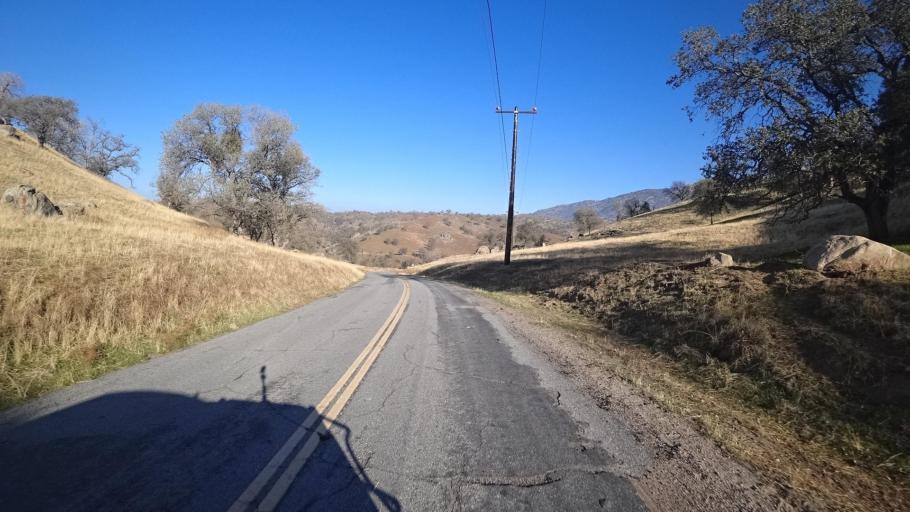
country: US
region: California
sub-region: Kern County
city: Alta Sierra
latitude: 35.7257
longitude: -118.8100
